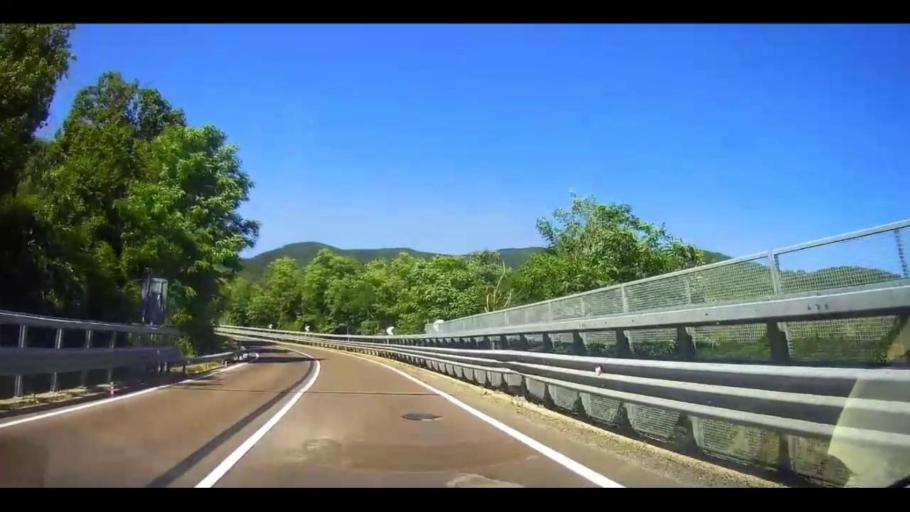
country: IT
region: Calabria
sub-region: Provincia di Cosenza
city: Spezzano Piccolo
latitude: 39.2919
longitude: 16.3504
